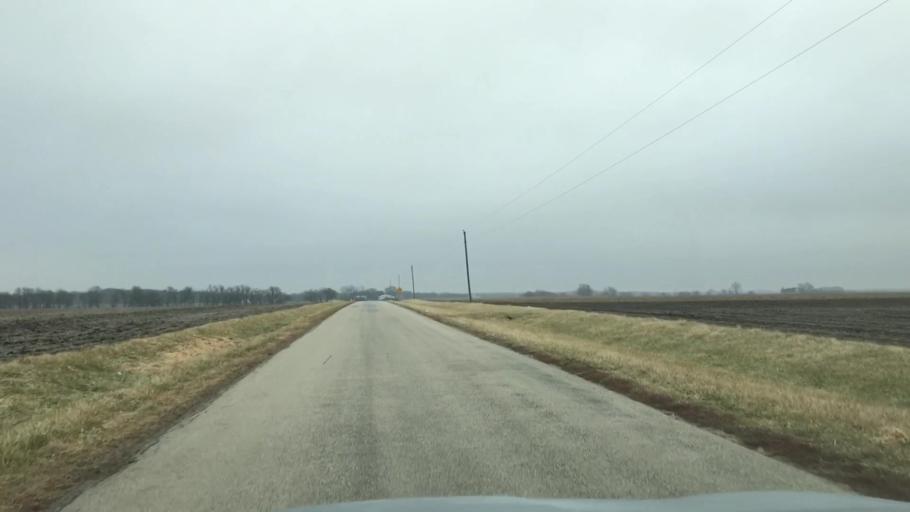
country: US
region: Illinois
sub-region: McLean County
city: Hudson
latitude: 40.6277
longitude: -88.9506
